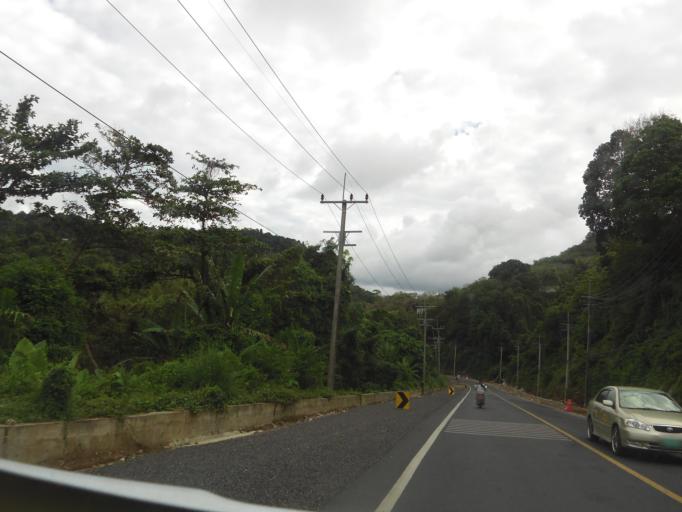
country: TH
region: Phuket
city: Ban Karon
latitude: 7.8642
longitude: 98.2843
